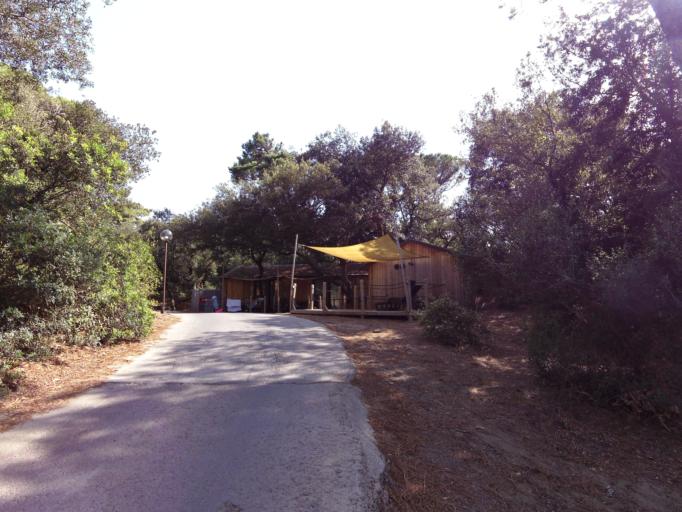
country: IT
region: Tuscany
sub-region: Provincia di Livorno
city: Donoratico
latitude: 43.1548
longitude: 10.5425
